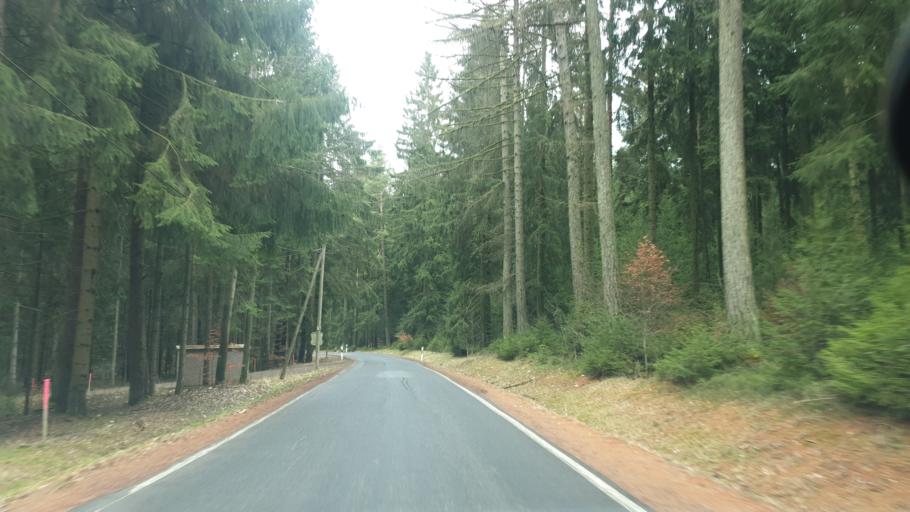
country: DE
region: Saxony
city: Bad Elster
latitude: 50.2911
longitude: 12.2046
